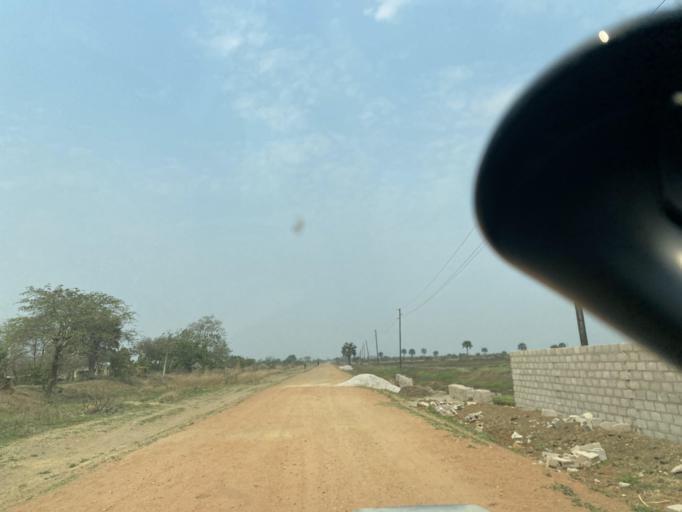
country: ZM
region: Lusaka
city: Kafue
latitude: -15.6733
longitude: 28.0171
